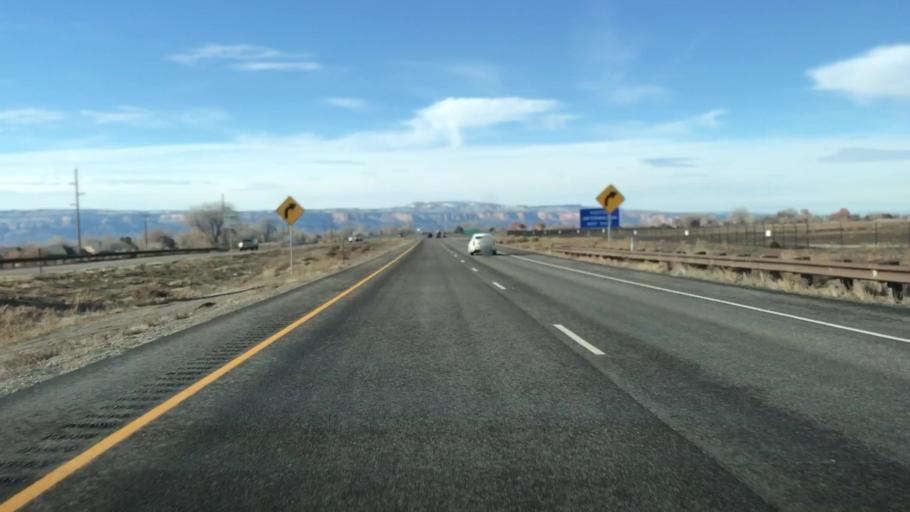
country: US
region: Colorado
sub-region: Mesa County
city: Fruitvale
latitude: 39.1058
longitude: -108.5259
